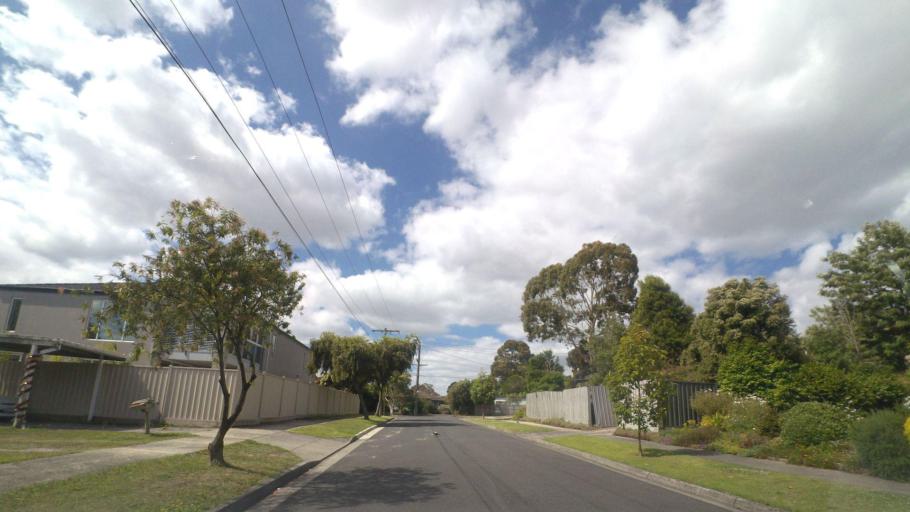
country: AU
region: Victoria
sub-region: Knox
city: Bayswater
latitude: -37.8654
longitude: 145.2588
